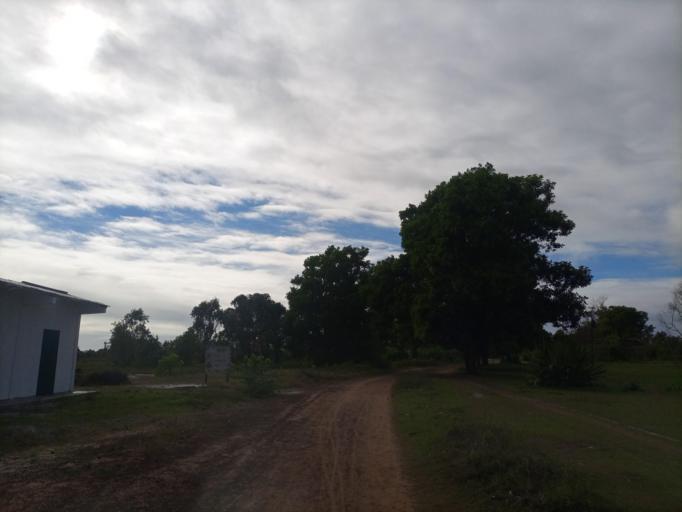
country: MG
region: Anosy
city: Fort Dauphin
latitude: -24.7793
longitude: 47.1818
